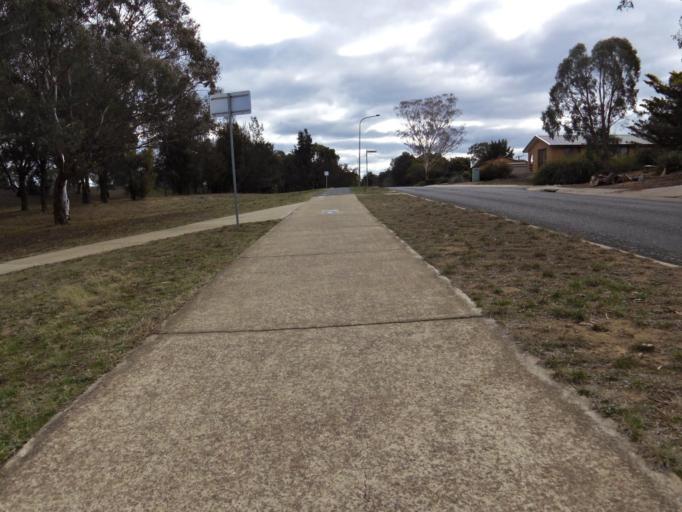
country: AU
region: Australian Capital Territory
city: Kaleen
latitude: -35.2359
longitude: 149.0988
